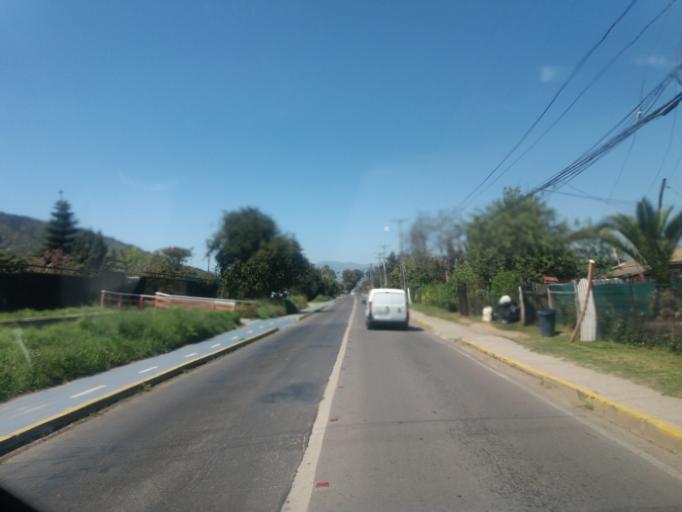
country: CL
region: Valparaiso
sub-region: Provincia de Marga Marga
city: Limache
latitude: -32.9795
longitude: -71.2844
